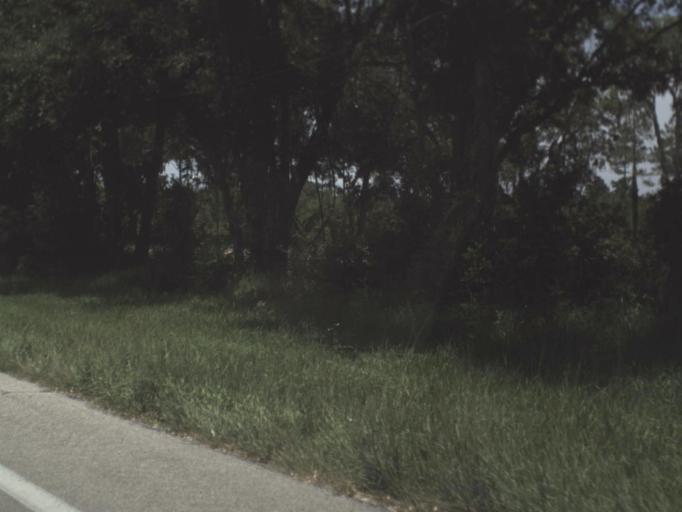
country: US
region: Florida
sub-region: Gilchrist County
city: Trenton
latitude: 29.6272
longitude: -82.8221
